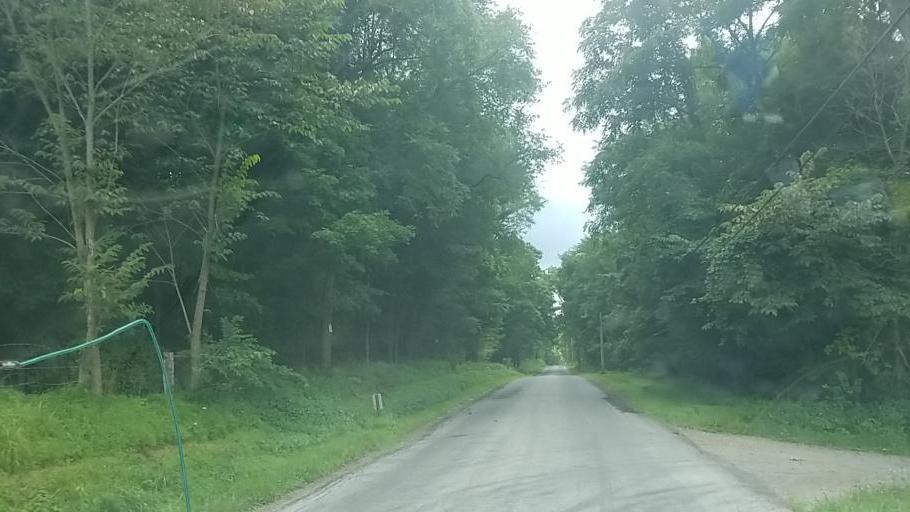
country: US
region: Ohio
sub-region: Muskingum County
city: Frazeysburg
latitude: 40.2099
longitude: -82.2596
